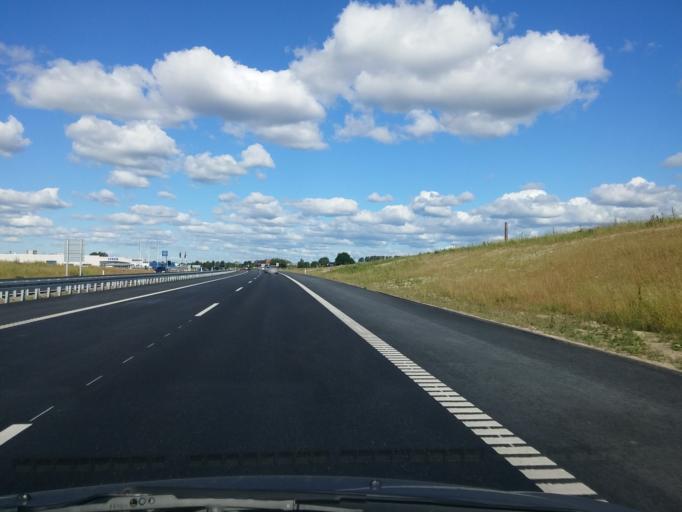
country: DK
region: South Denmark
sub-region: Odense Kommune
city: Hojby
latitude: 55.3500
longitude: 10.4216
